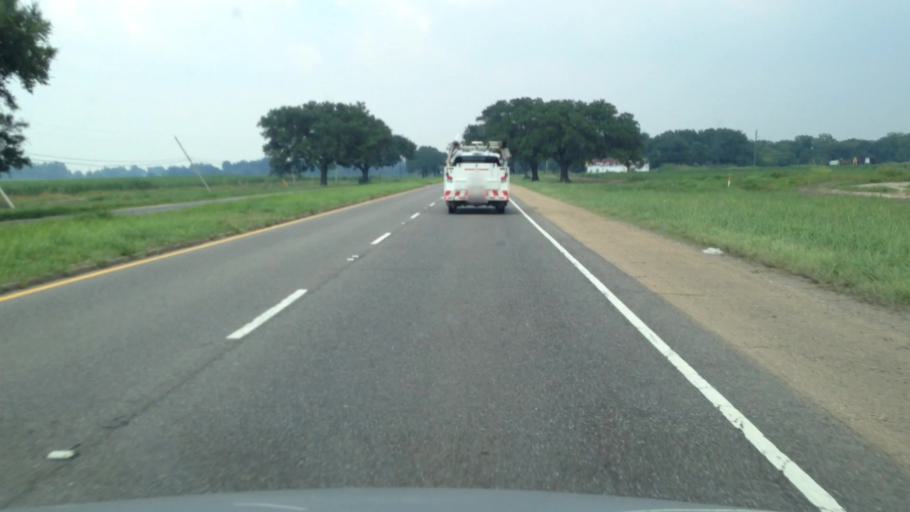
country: US
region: Louisiana
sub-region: West Baton Rouge Parish
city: Port Allen
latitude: 30.5003
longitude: -91.2395
